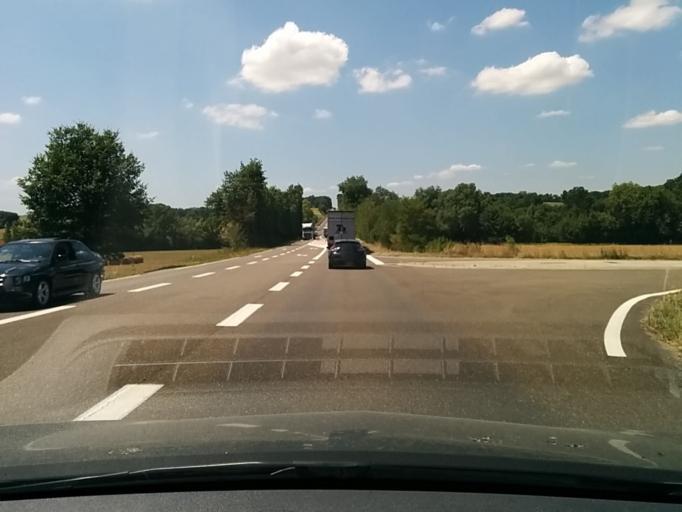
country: FR
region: Midi-Pyrenees
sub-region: Departement du Gers
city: Vic-Fezensac
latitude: 43.7518
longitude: 0.2654
